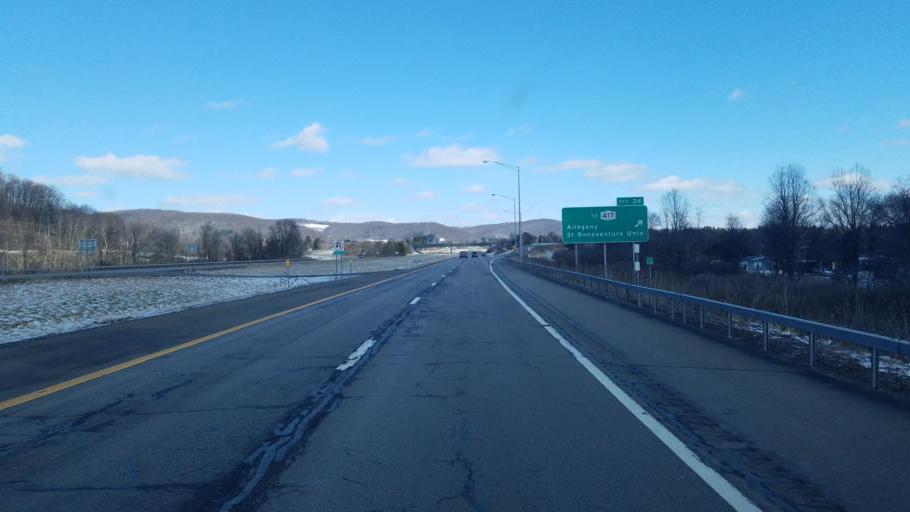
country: US
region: New York
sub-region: Cattaraugus County
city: Allegany
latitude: 42.1026
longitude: -78.5152
